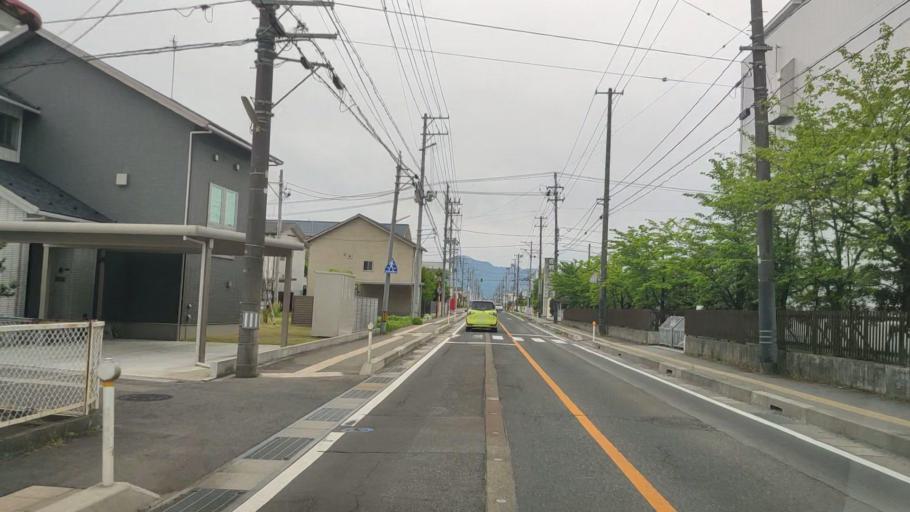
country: JP
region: Niigata
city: Gosen
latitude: 37.7345
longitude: 139.1766
